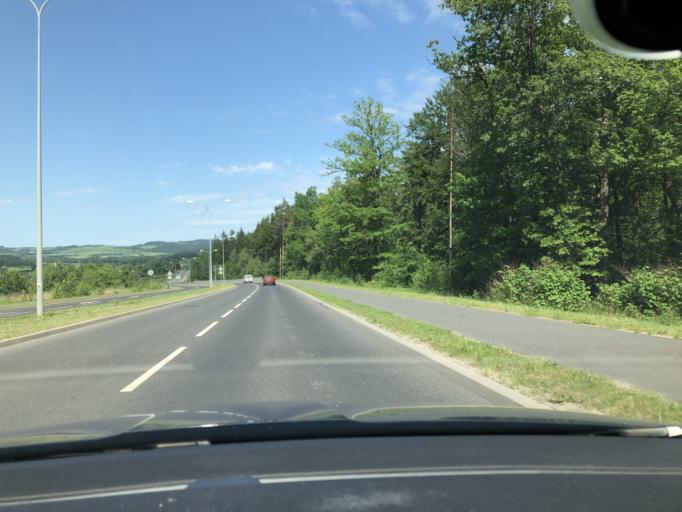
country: PL
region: Lower Silesian Voivodeship
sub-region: Jelenia Gora
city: Jelenia Gora
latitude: 50.8922
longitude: 15.7643
